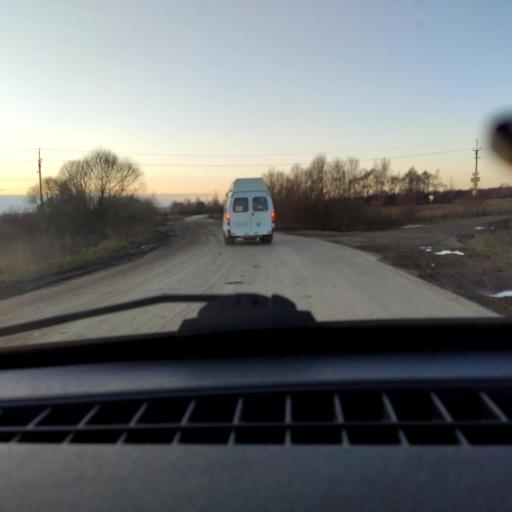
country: RU
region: Bashkortostan
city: Ufa
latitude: 54.7005
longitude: 56.1270
